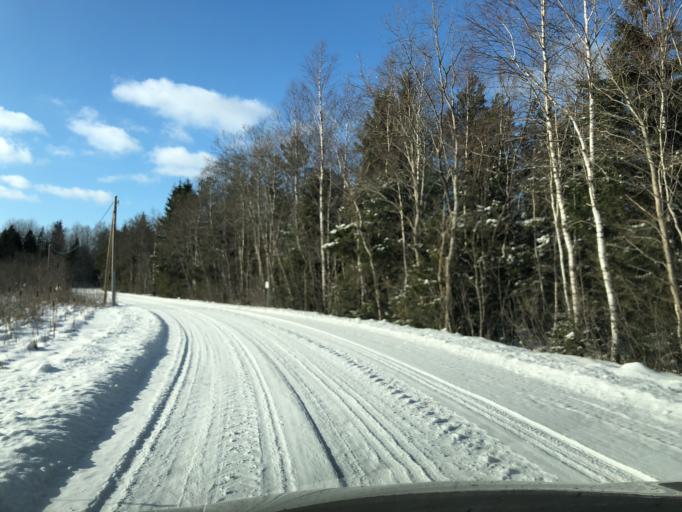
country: EE
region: Jaervamaa
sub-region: Paide linn
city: Paide
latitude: 59.0604
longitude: 25.4985
